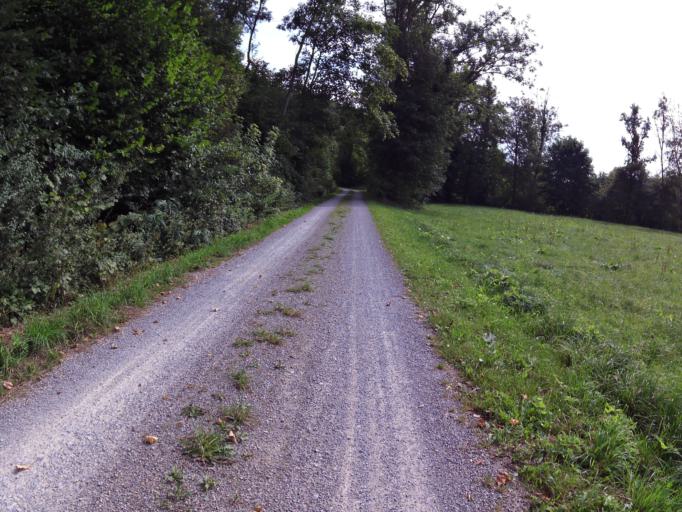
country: DE
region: Baden-Wuerttemberg
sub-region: Freiburg Region
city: Sulz am Neckar
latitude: 48.3477
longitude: 8.5937
